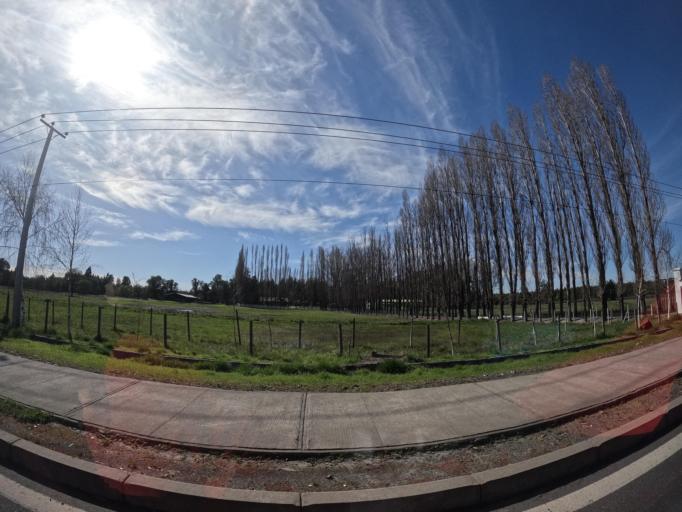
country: CL
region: Biobio
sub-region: Provincia de Biobio
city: Cabrero
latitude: -37.0303
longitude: -72.4284
